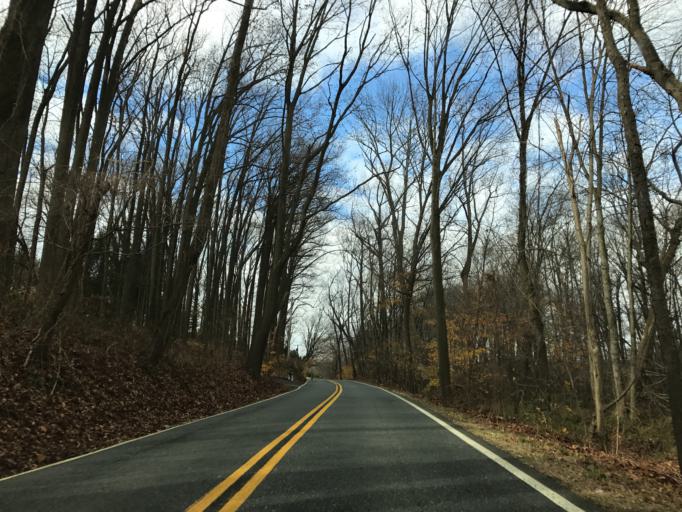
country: US
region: Maryland
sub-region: Baltimore County
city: Perry Hall
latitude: 39.4876
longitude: -76.5109
